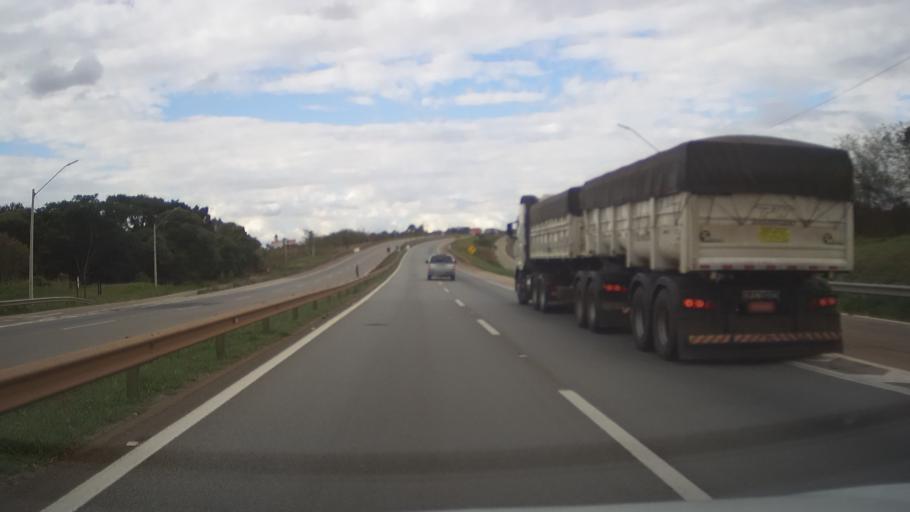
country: BR
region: Minas Gerais
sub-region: Itauna
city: Itauna
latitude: -20.3068
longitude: -44.4478
